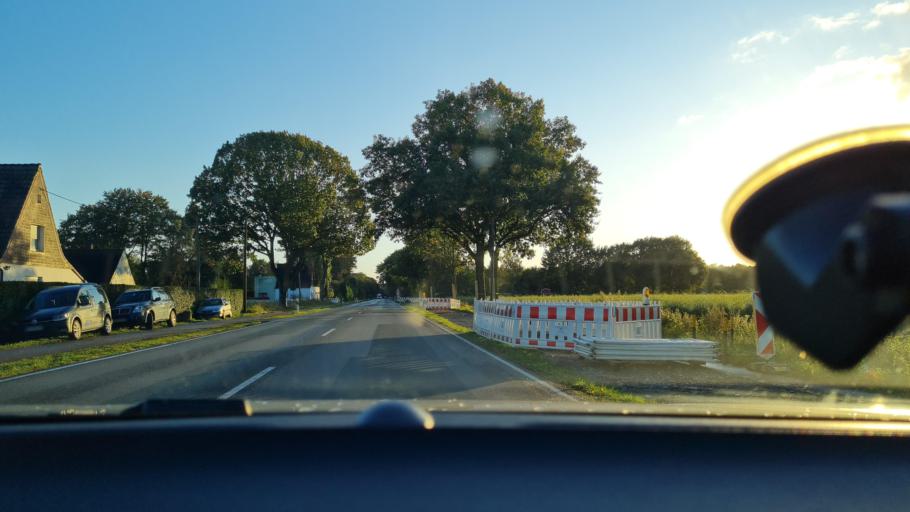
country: DE
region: North Rhine-Westphalia
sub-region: Regierungsbezirk Dusseldorf
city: Voerde
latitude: 51.6274
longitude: 6.7072
